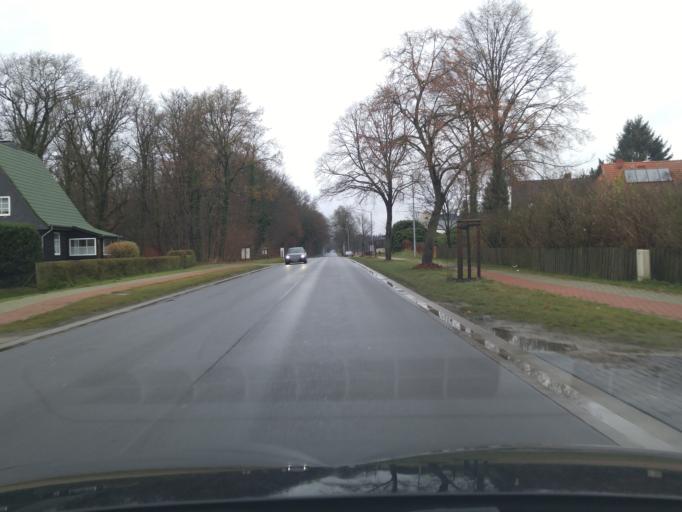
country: DE
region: Lower Saxony
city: Sprakensehl
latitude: 52.7694
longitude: 10.4936
